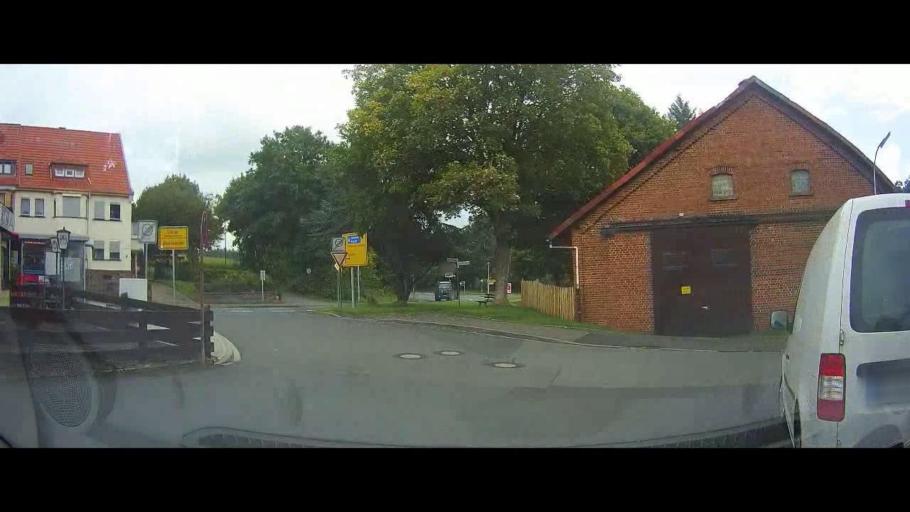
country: DE
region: Lower Saxony
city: Uslar
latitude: 51.6535
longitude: 9.6485
